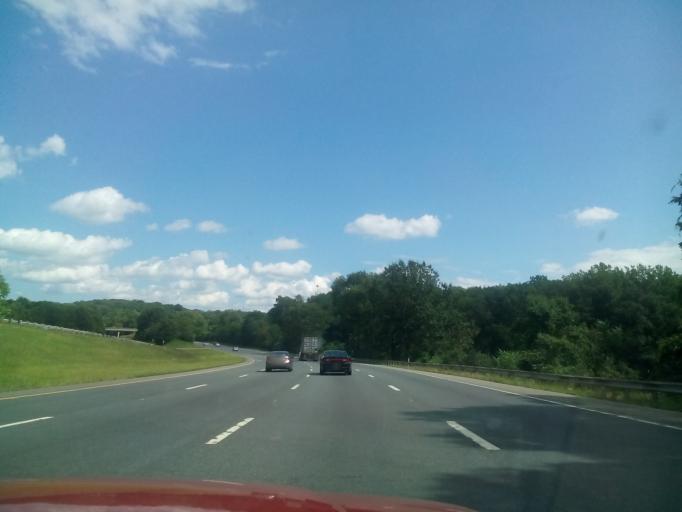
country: US
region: New Jersey
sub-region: Warren County
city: Belvidere
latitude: 40.9230
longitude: -75.0649
